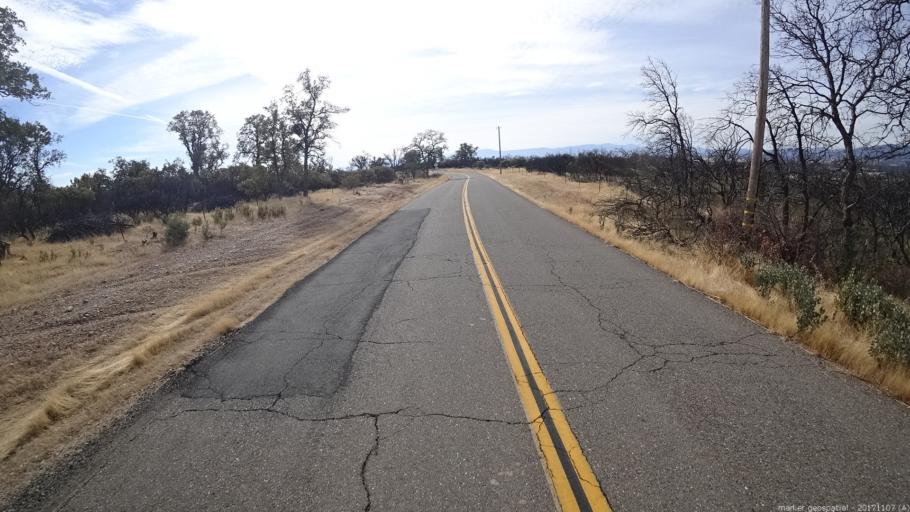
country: US
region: California
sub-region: Shasta County
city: Shasta
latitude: 40.4675
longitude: -122.5415
